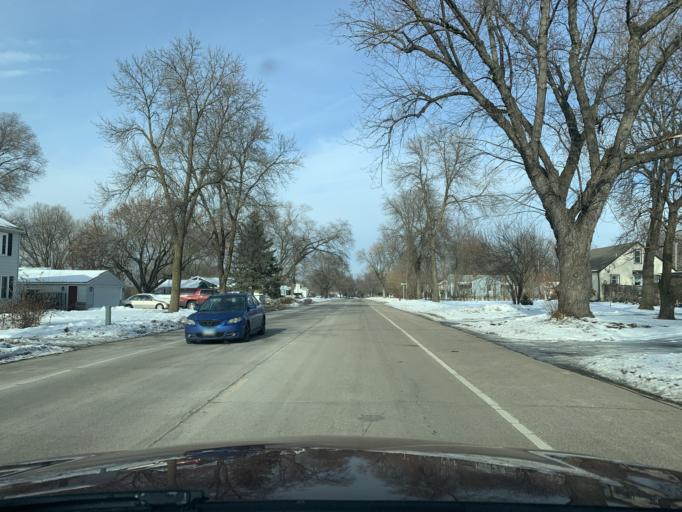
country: US
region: Minnesota
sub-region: Washington County
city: Saint Paul Park
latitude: 44.8377
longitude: -92.9906
